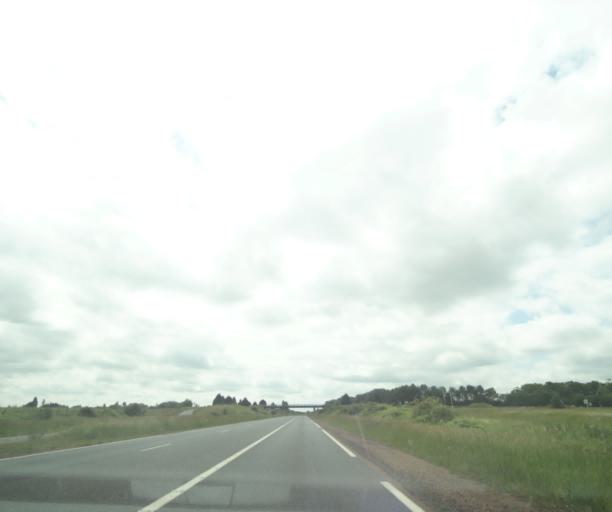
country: FR
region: Poitou-Charentes
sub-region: Departement des Deux-Sevres
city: Saint-Varent
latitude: 46.8298
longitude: -0.2058
